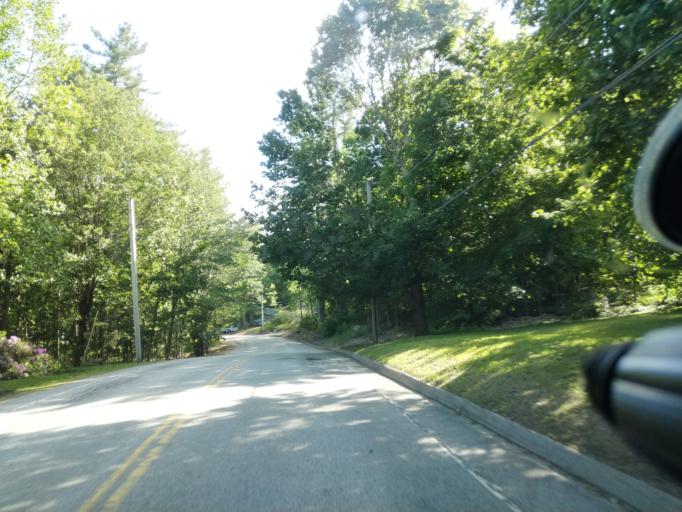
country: US
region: Maine
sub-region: Cumberland County
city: Falmouth
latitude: 43.7371
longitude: -70.3051
